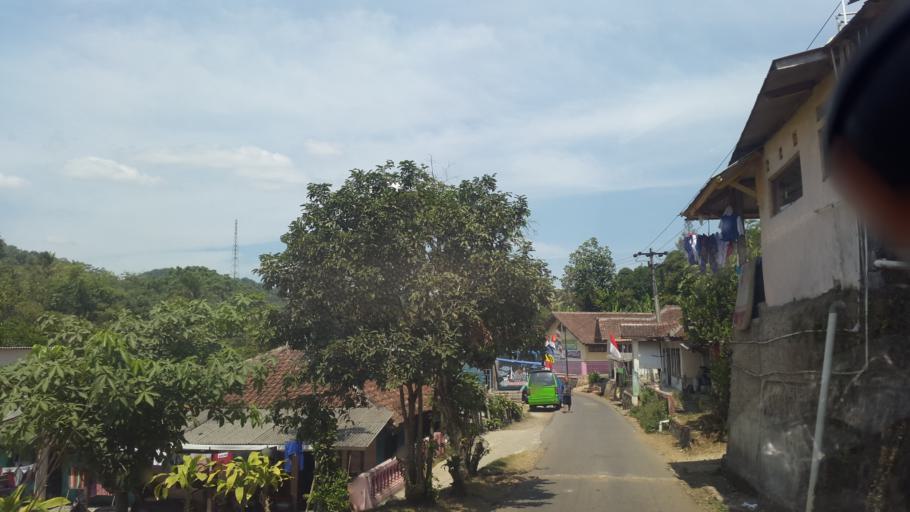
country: ID
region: West Java
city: Sindangsari
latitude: -6.8946
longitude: 106.6512
